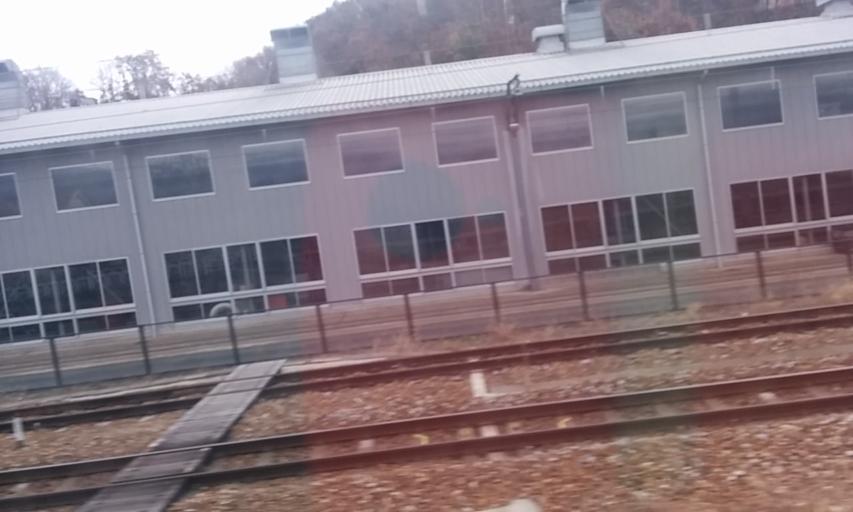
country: JP
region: Nagano
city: Nagano-shi
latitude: 36.5307
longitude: 138.1289
